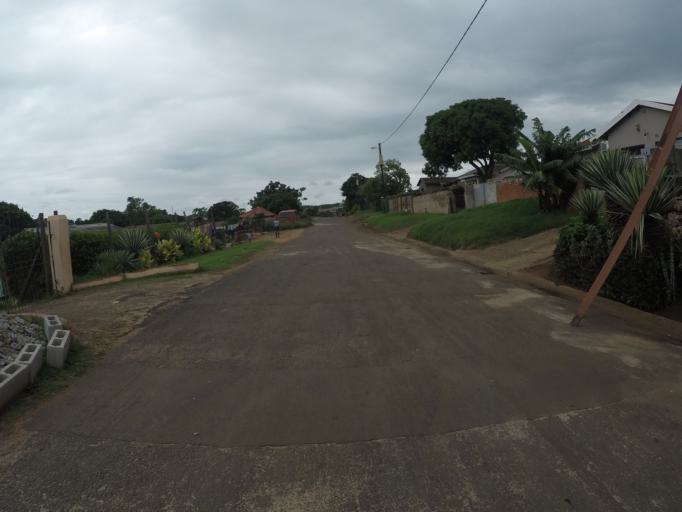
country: ZA
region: KwaZulu-Natal
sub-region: uThungulu District Municipality
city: Empangeni
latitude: -28.7731
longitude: 31.8561
